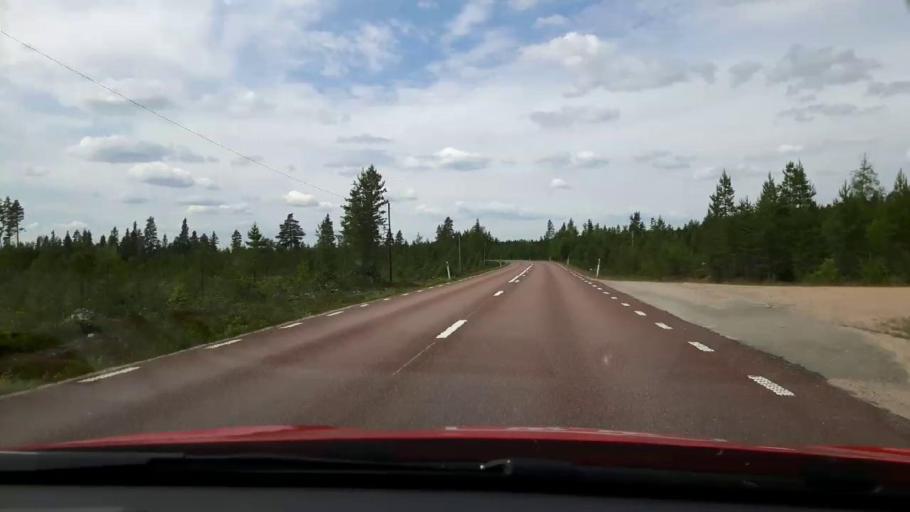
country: SE
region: Jaemtland
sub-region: Harjedalens Kommun
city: Sveg
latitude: 62.0550
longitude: 14.5491
